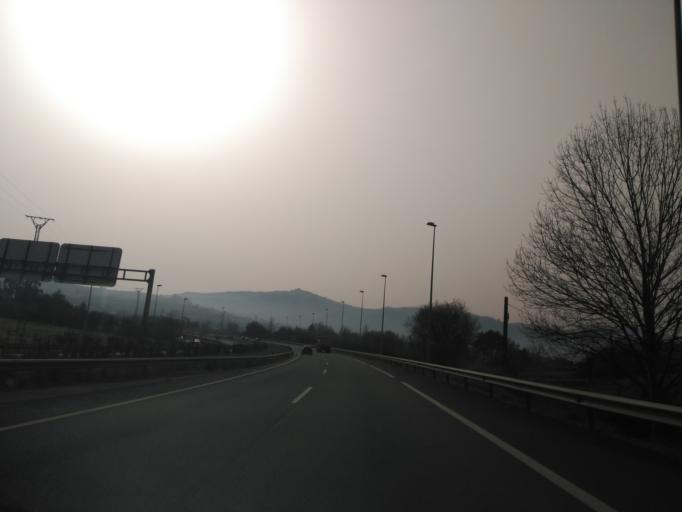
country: ES
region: Cantabria
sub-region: Provincia de Cantabria
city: Torrelavega
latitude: 43.3532
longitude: -4.0373
